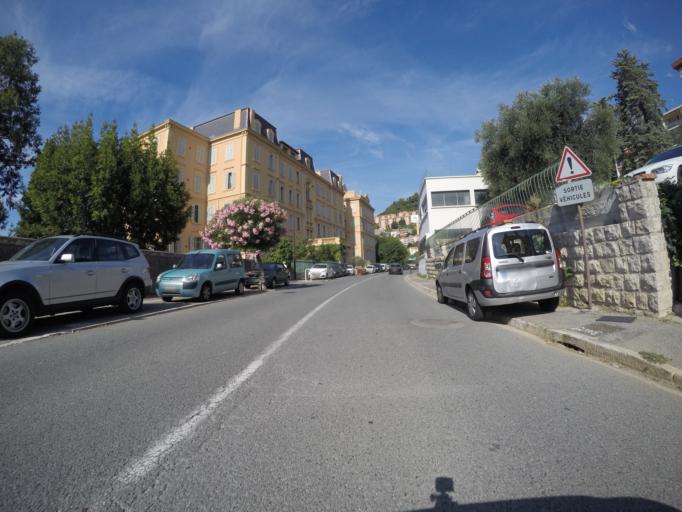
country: FR
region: Provence-Alpes-Cote d'Azur
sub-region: Departement des Alpes-Maritimes
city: Grasse
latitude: 43.6634
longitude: 6.9289
